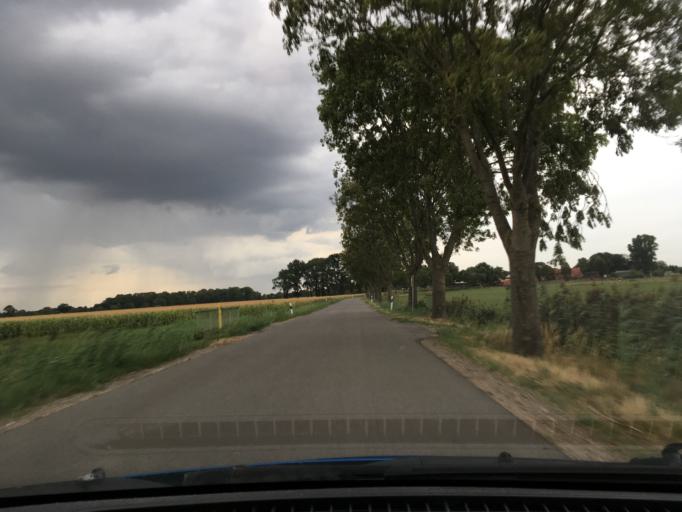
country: DE
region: Schleswig-Holstein
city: Lanze
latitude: 53.3813
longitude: 10.5983
